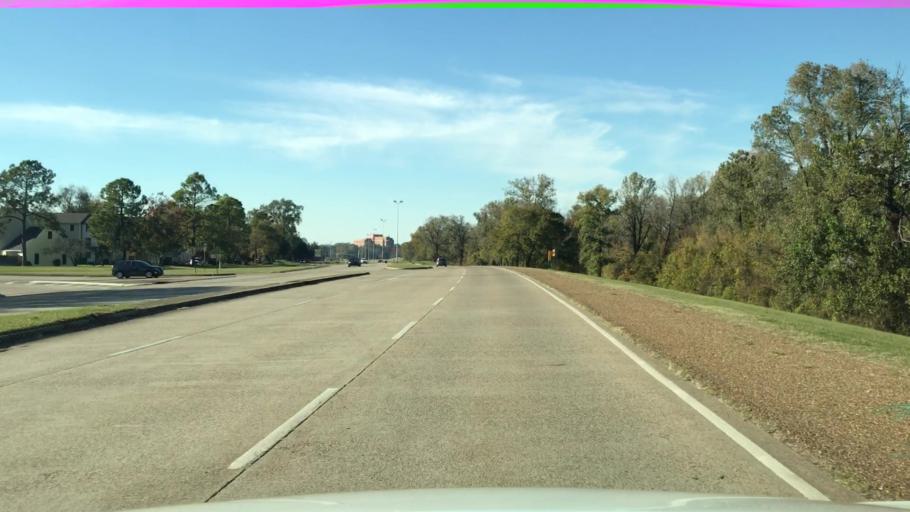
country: US
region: Louisiana
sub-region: Bossier Parish
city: Bossier City
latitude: 32.4915
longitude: -93.7016
